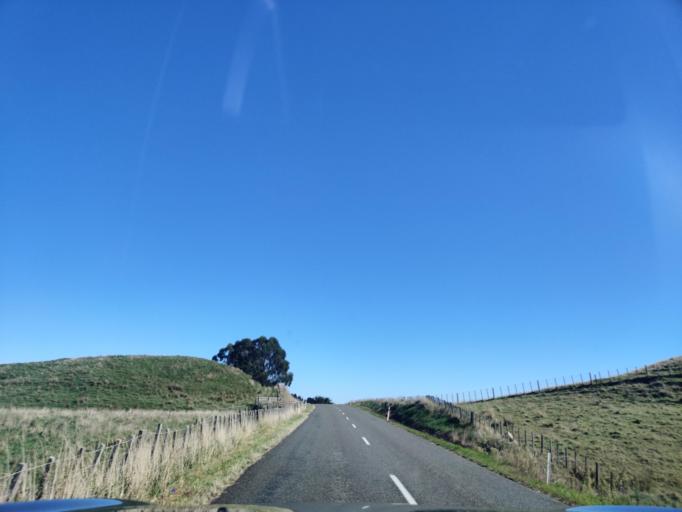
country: NZ
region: Manawatu-Wanganui
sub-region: Palmerston North City
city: Palmerston North
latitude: -40.2587
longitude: 175.7104
